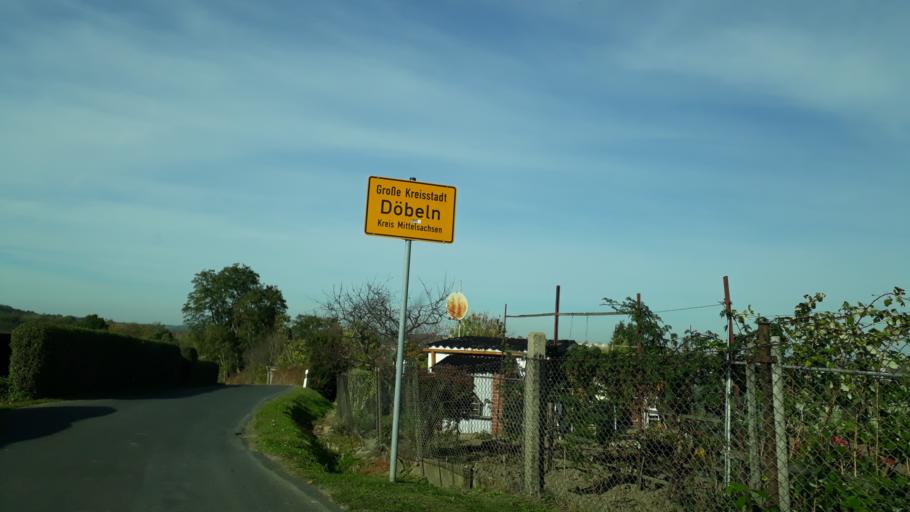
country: DE
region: Saxony
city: Niederstriegis
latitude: 51.1068
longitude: 13.1422
